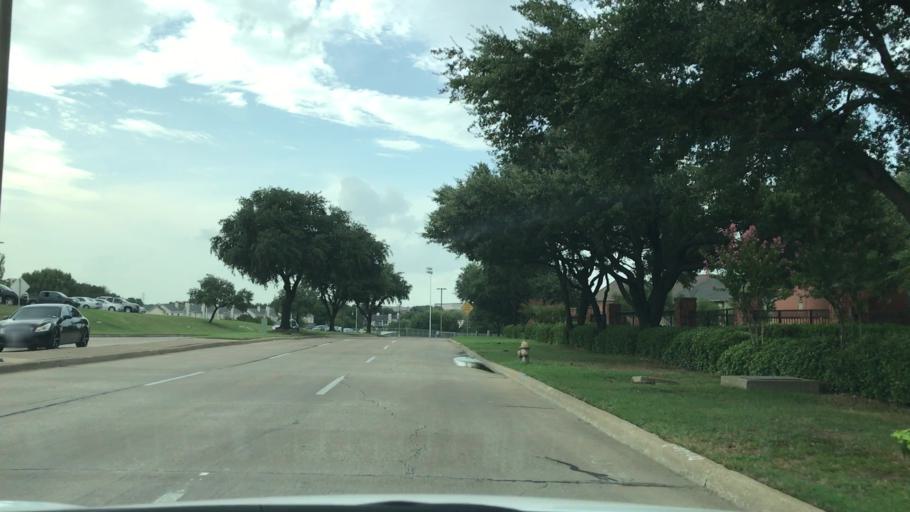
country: US
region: Texas
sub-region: Dallas County
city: Irving
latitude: 32.8618
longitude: -96.9766
